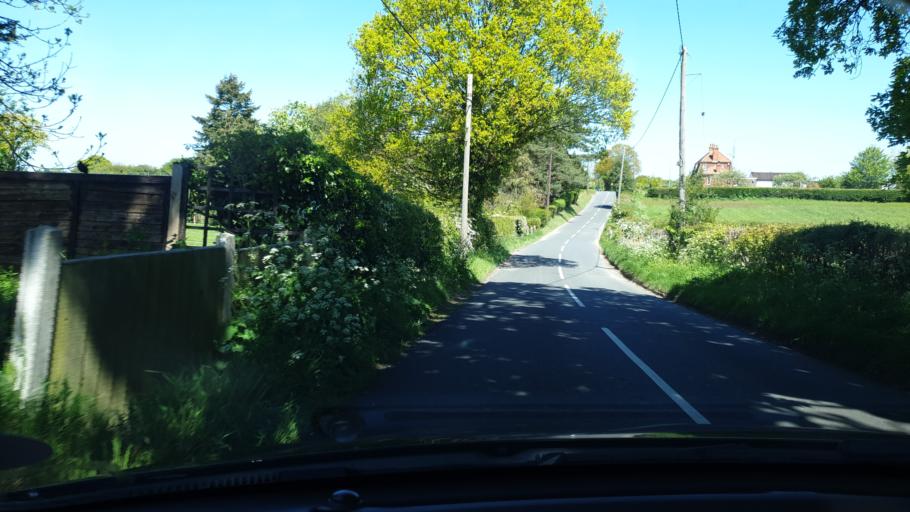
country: GB
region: England
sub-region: Essex
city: Little Clacton
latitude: 51.8625
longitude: 1.1200
